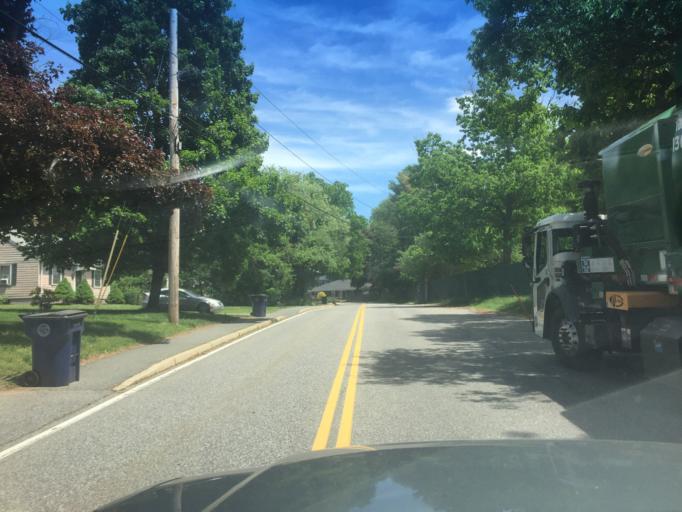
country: US
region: Massachusetts
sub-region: Norfolk County
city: Medway
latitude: 42.1408
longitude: -71.4228
